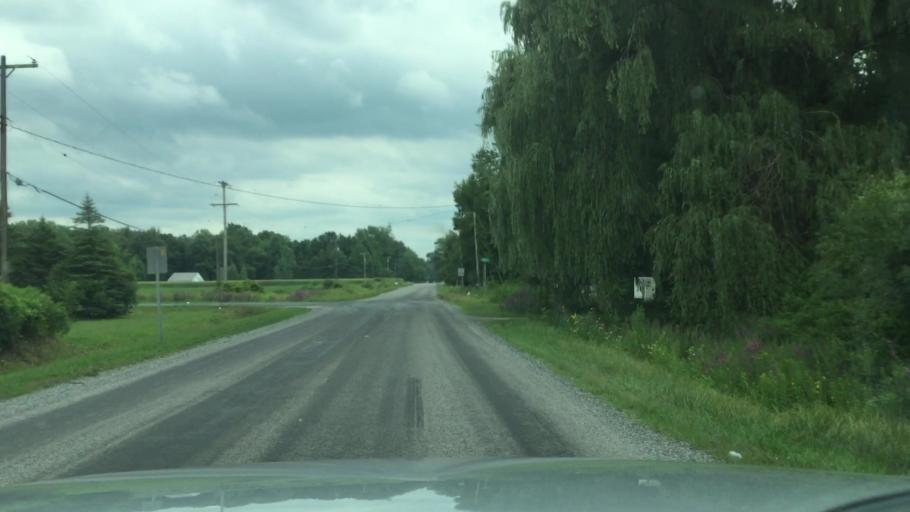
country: US
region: Michigan
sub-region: Saginaw County
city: Bridgeport
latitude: 43.3220
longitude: -83.8856
